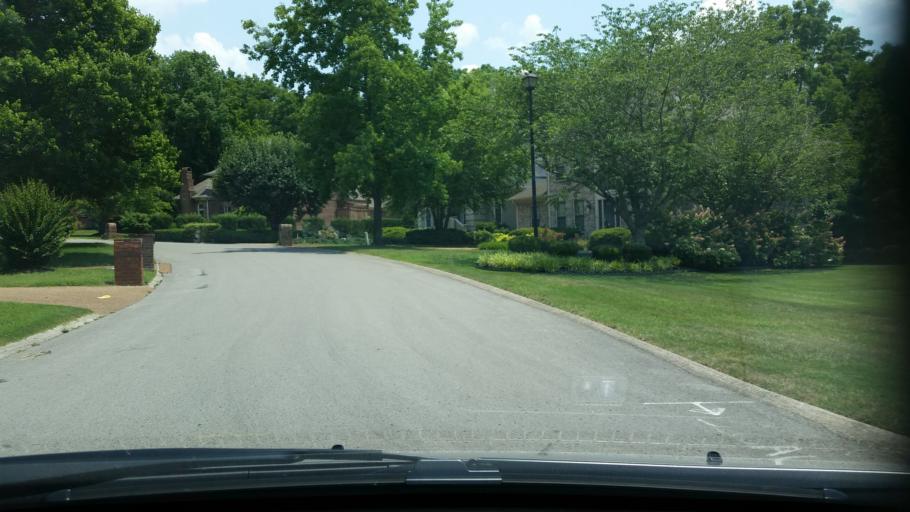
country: US
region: Tennessee
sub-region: Williamson County
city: Brentwood Estates
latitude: 35.9767
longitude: -86.7569
